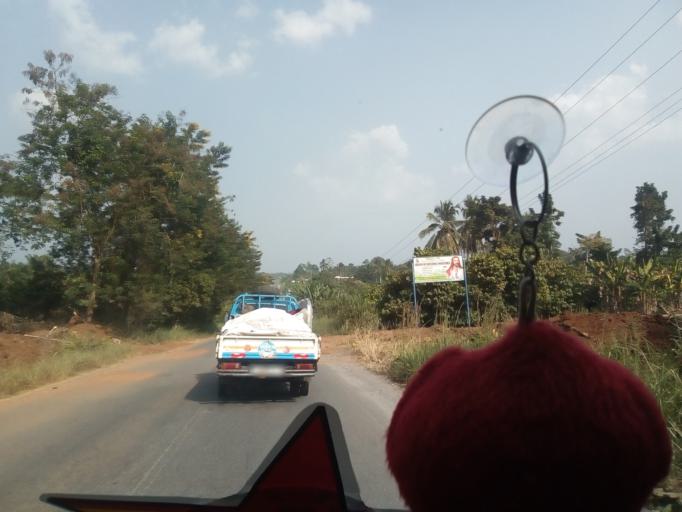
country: GH
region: Eastern
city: Suhum
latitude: 6.0437
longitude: -0.4270
